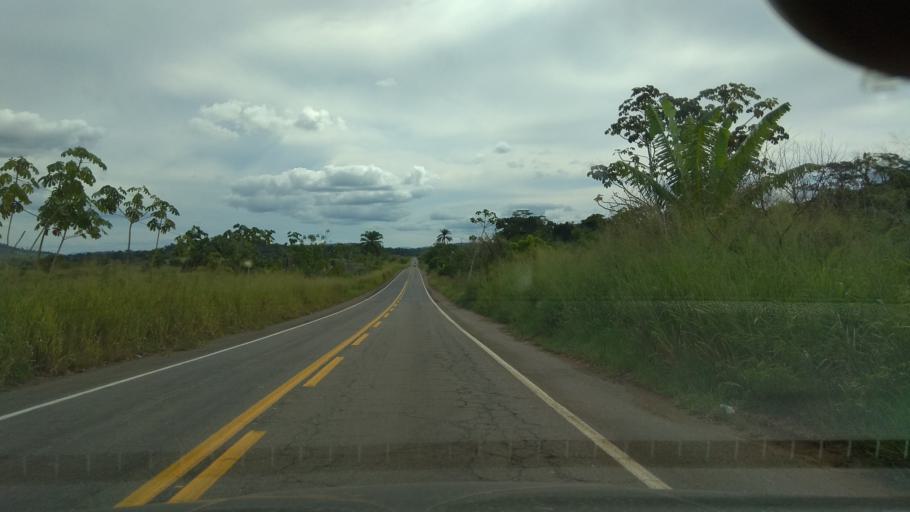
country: BR
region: Bahia
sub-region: Ubata
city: Ubata
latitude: -14.1962
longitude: -39.6272
